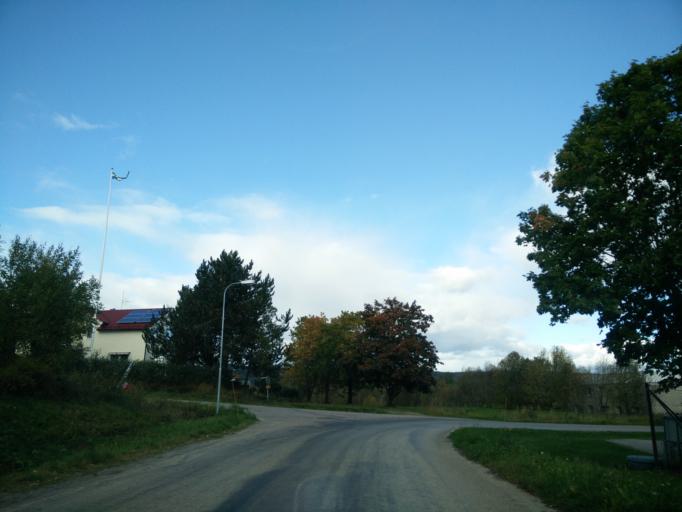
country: SE
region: Vaesternorrland
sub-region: Sundsvalls Kommun
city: Matfors
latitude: 62.3452
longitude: 17.0097
